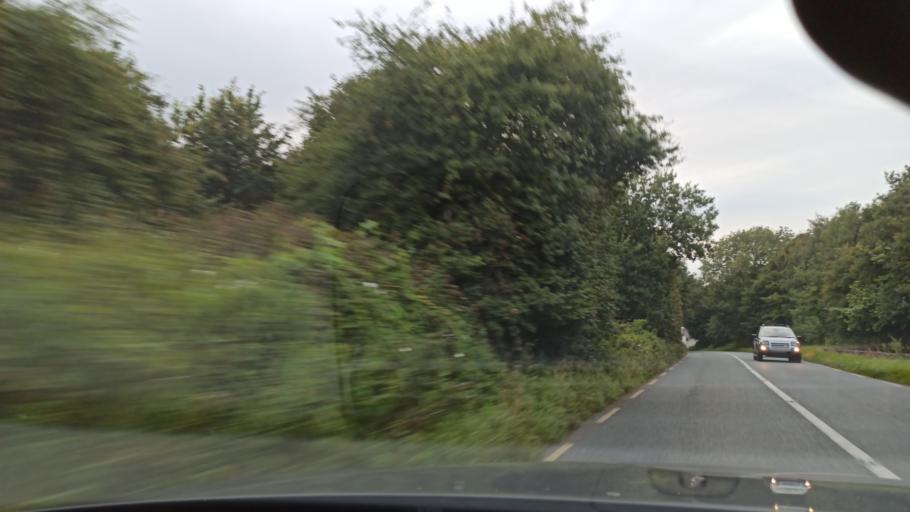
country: IE
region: Munster
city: Cashel
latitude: 52.4757
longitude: -7.8479
